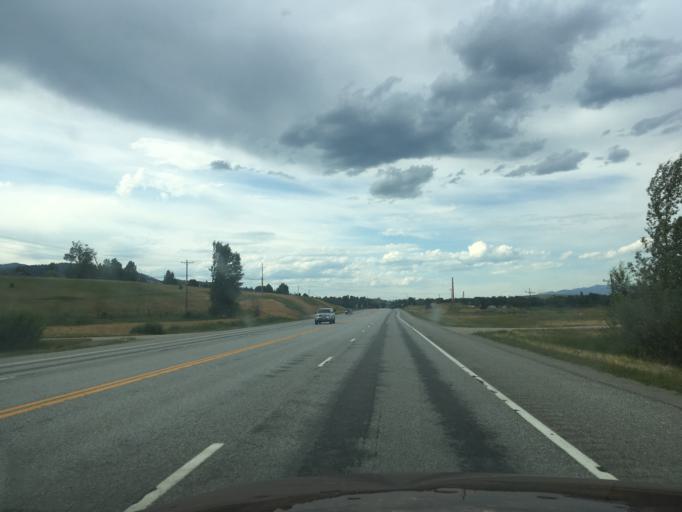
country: US
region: Montana
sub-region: Missoula County
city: Lolo
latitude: 46.7368
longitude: -114.0806
